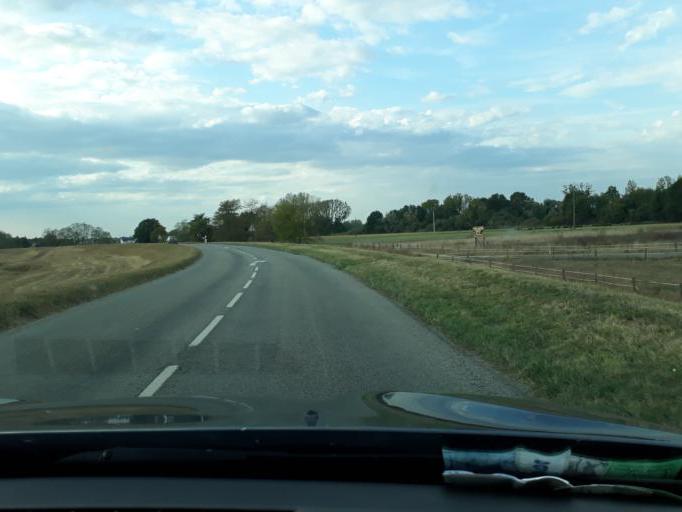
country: FR
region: Centre
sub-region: Departement du Loiret
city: Saint-Benoit-sur-Loire
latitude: 47.8304
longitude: 2.2861
